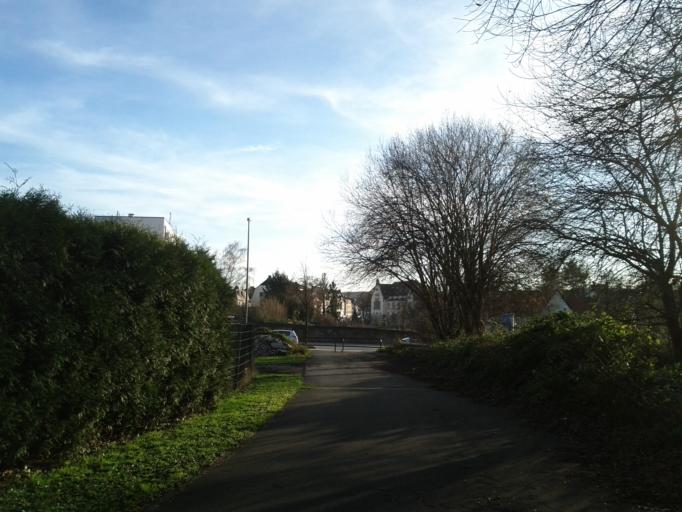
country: DE
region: North Rhine-Westphalia
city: Schwerte
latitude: 51.4944
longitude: 7.5548
